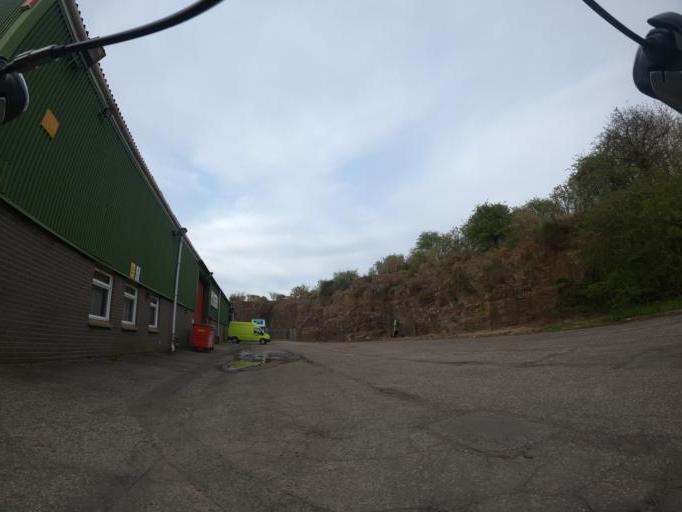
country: GB
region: Scotland
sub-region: Edinburgh
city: Currie
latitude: 55.9440
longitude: -3.3184
